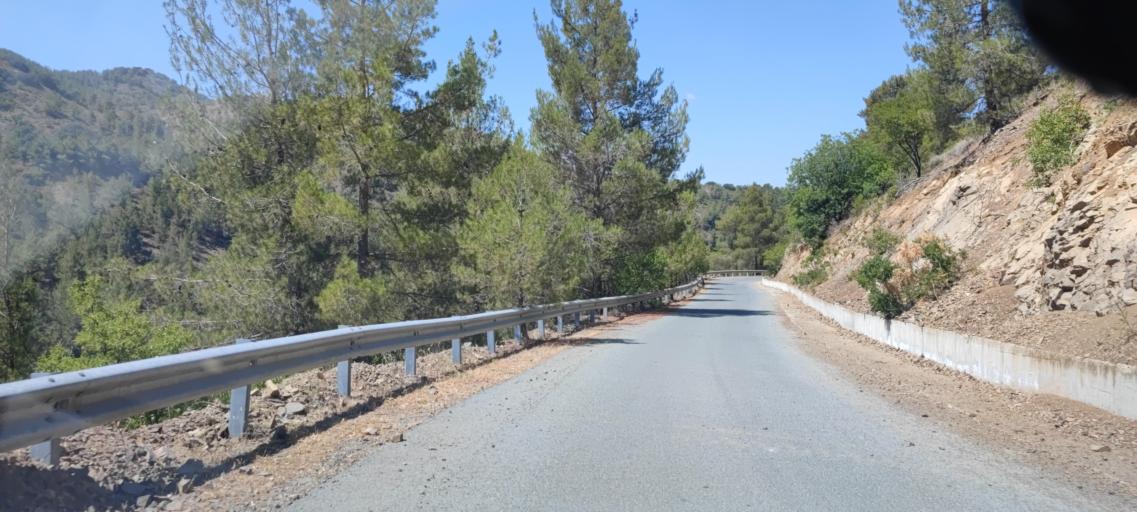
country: CY
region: Lefkosia
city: Kakopetria
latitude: 34.9254
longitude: 32.8014
